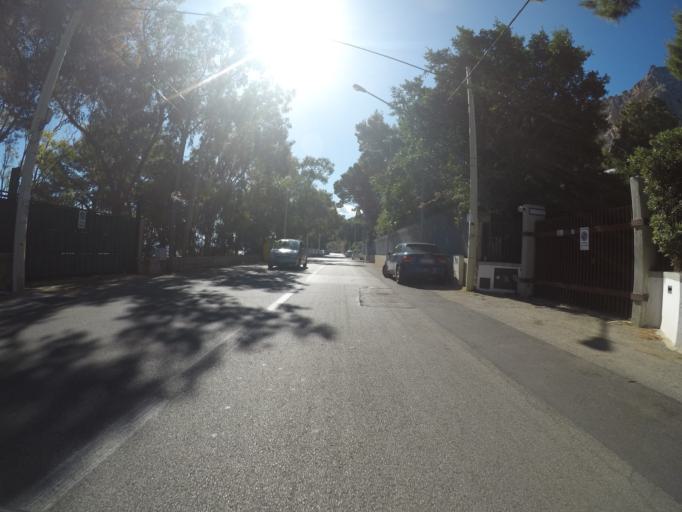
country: IT
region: Sicily
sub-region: Palermo
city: Palermo
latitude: 38.1887
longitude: 13.3595
